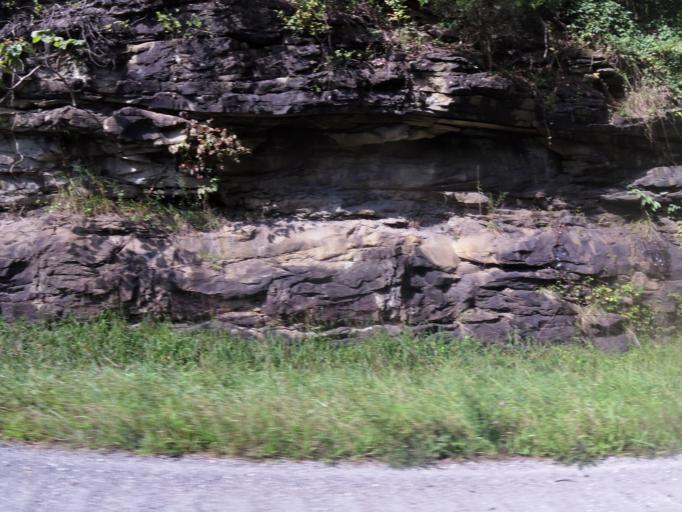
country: US
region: Kentucky
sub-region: Bell County
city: Pineville
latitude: 36.7334
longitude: -83.6451
